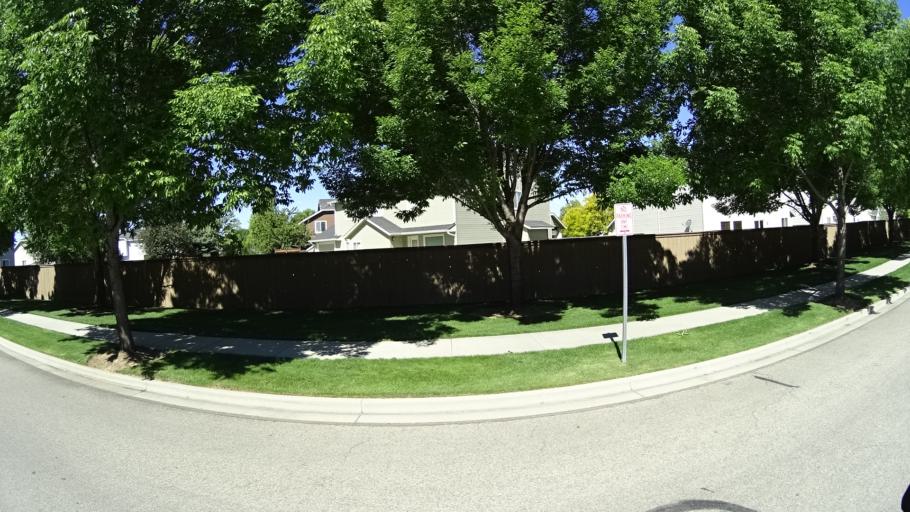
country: US
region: Idaho
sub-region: Ada County
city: Meridian
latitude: 43.6350
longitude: -116.3906
